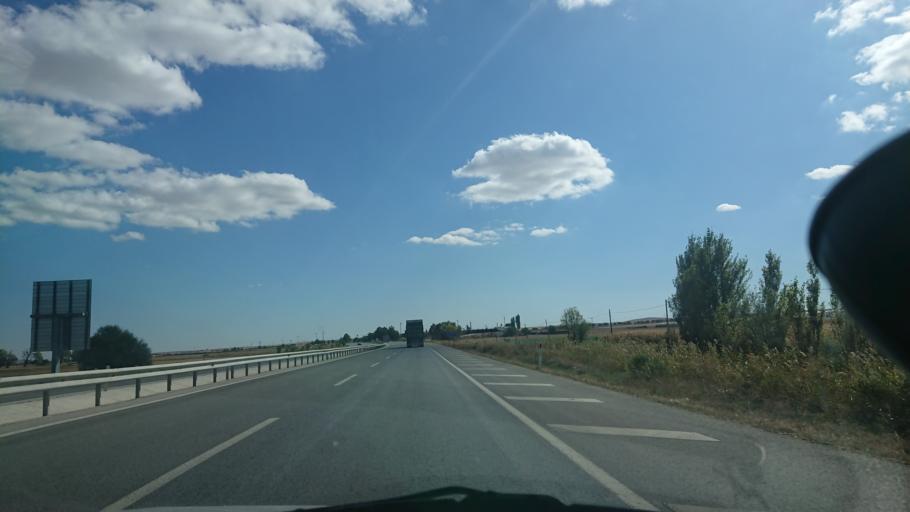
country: TR
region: Eskisehir
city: Mahmudiye
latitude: 39.5664
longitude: 30.9142
